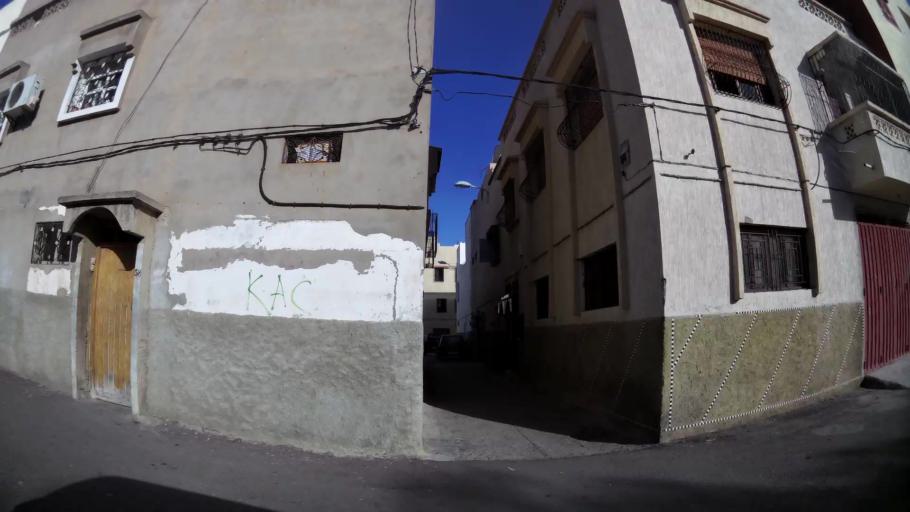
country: MA
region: Souss-Massa-Draa
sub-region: Agadir-Ida-ou-Tnan
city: Agadir
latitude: 30.4275
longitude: -9.5848
